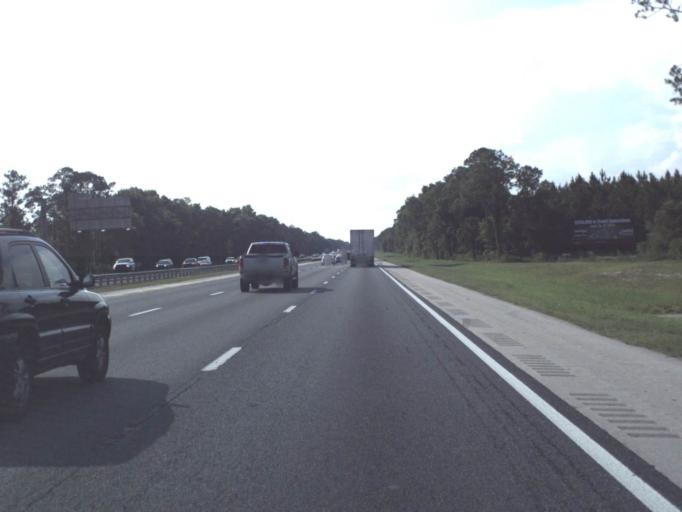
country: US
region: Florida
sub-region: Saint Johns County
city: Saint Augustine
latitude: 29.9322
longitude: -81.4221
